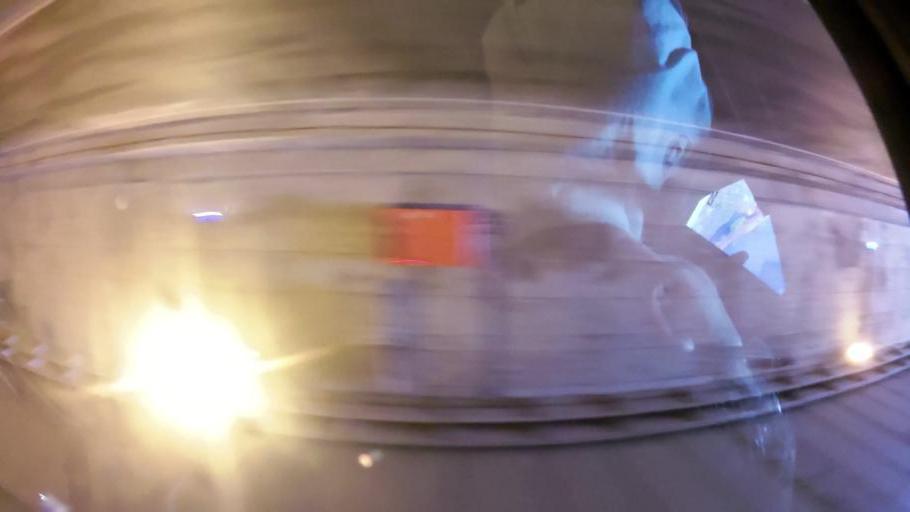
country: CO
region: Bolivar
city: Cartagena
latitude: 10.4455
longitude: -75.5237
